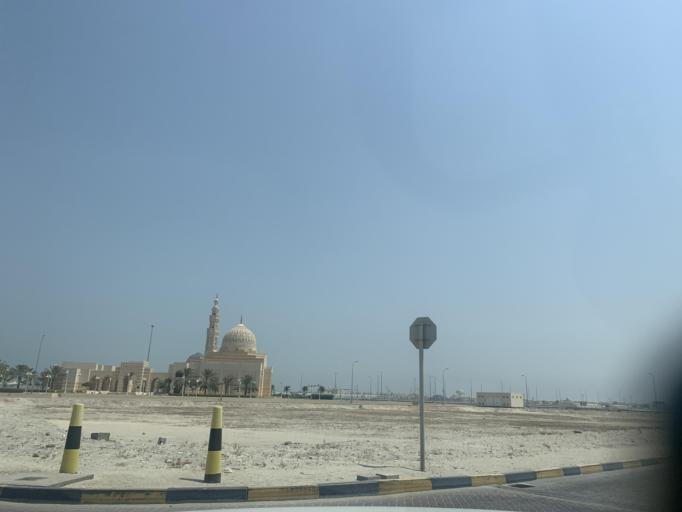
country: BH
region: Muharraq
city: Al Muharraq
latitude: 26.2972
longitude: 50.6404
